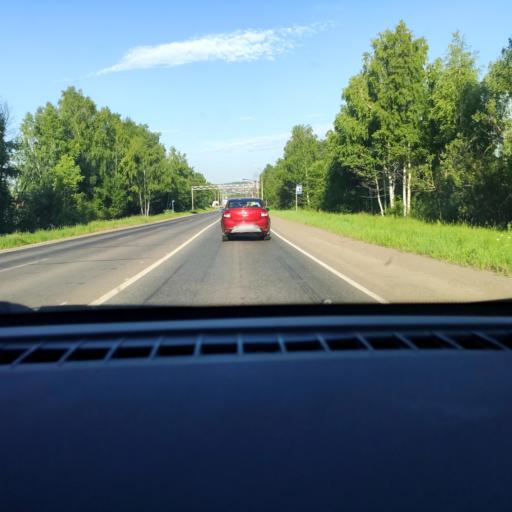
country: RU
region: Udmurtiya
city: Khokhryaki
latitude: 56.9146
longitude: 53.4031
